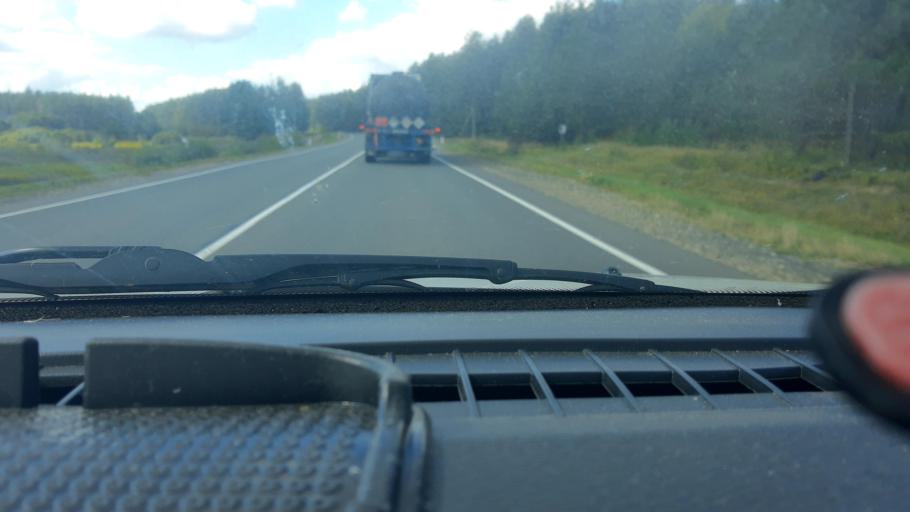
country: RU
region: Nizjnij Novgorod
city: Shatki
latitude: 55.1315
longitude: 44.2599
